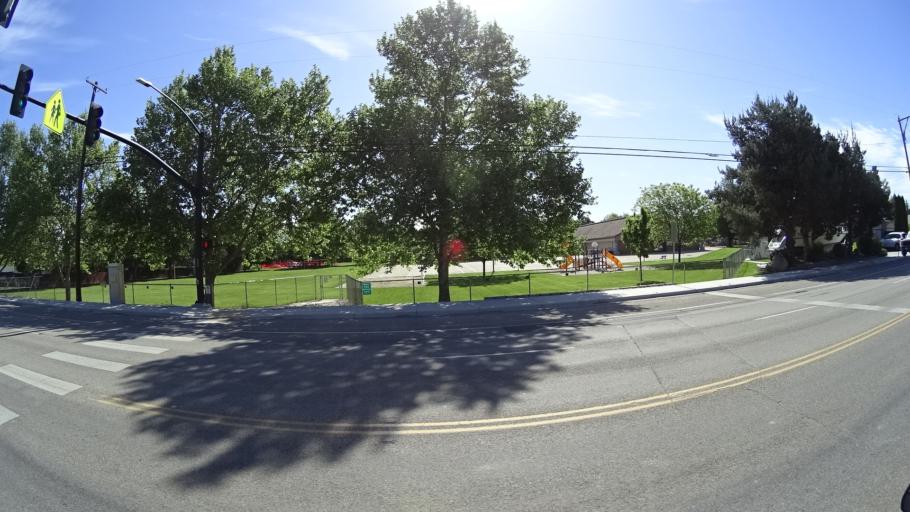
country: US
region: Idaho
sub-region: Ada County
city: Garden City
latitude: 43.5845
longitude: -116.2437
